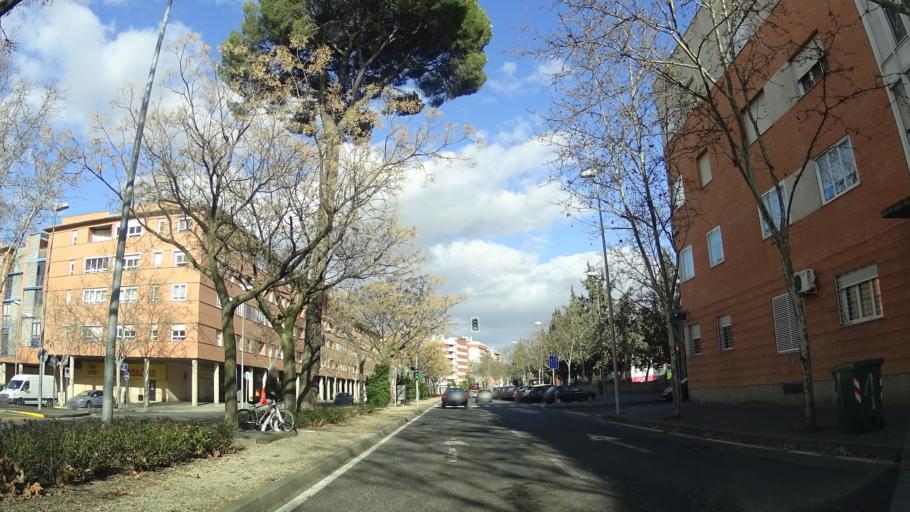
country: ES
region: Castille-La Mancha
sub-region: Provincia de Ciudad Real
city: Ciudad Real
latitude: 38.9794
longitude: -3.9317
